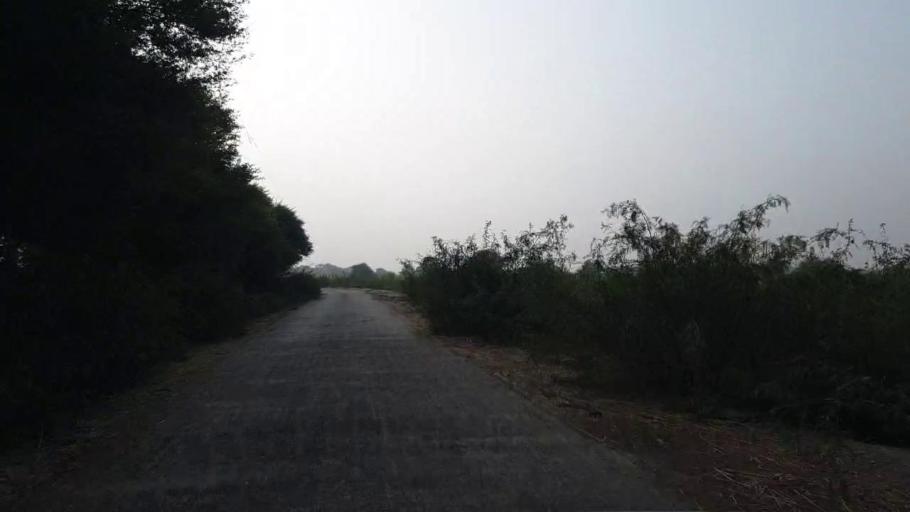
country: PK
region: Sindh
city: Tando Muhammad Khan
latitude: 25.1708
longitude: 68.6069
